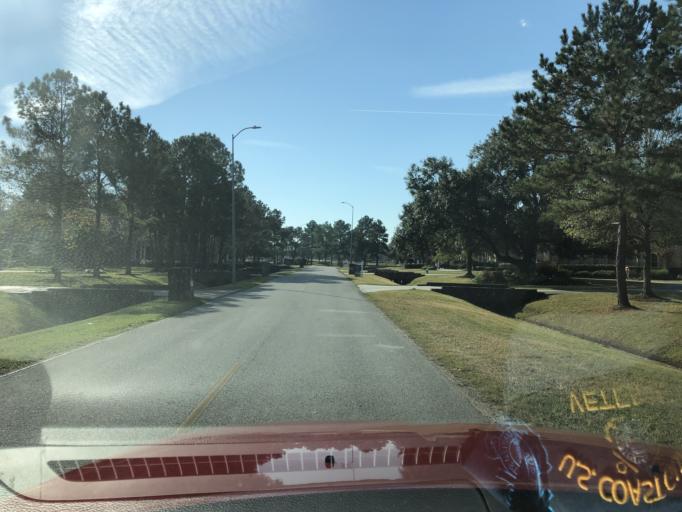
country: US
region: Texas
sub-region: Harris County
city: Tomball
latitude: 30.0387
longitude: -95.5592
